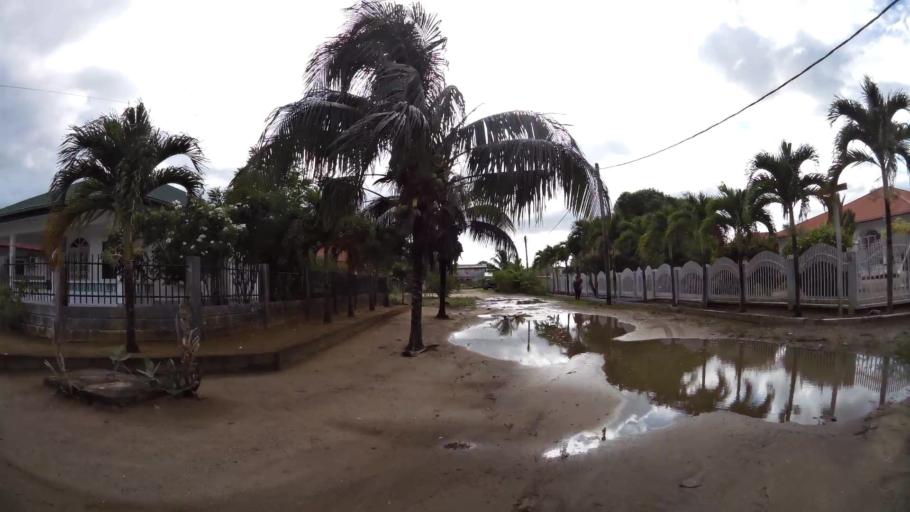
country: SR
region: Paramaribo
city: Paramaribo
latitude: 5.8474
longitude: -55.2319
